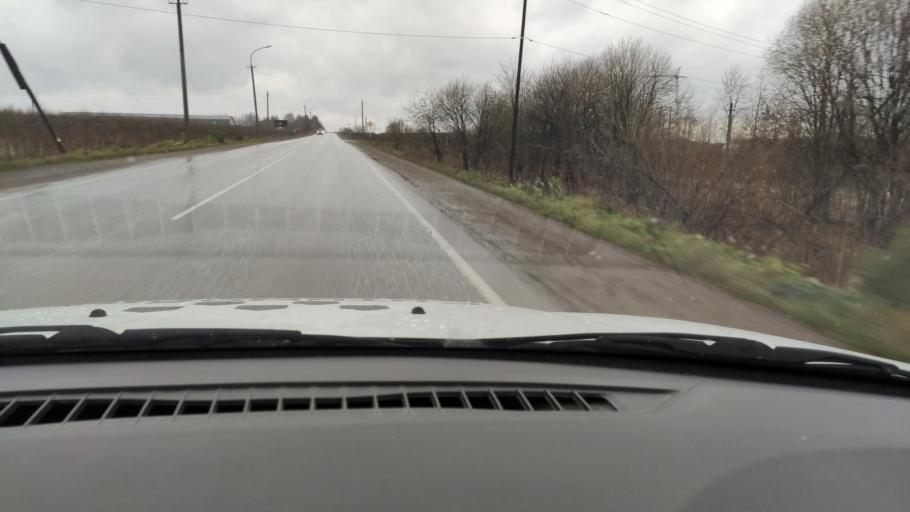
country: RU
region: Perm
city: Sylva
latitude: 58.0270
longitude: 56.7267
